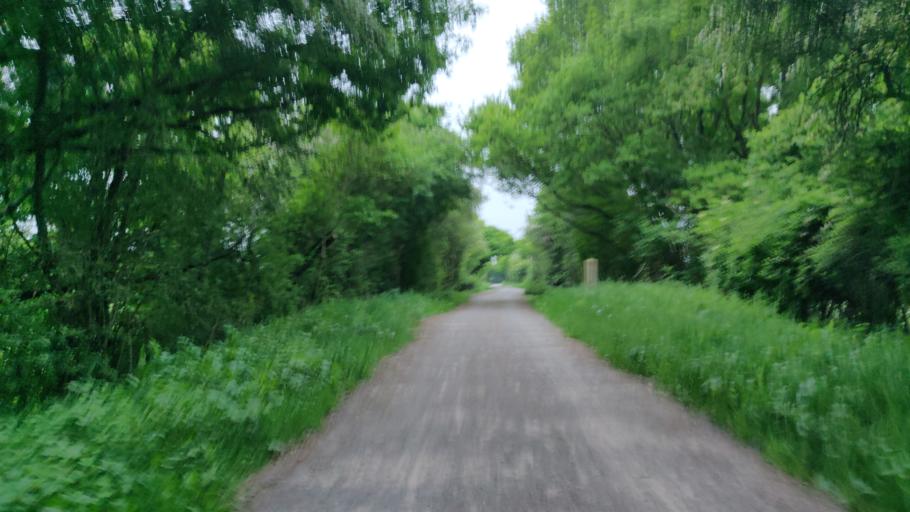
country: GB
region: England
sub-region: West Sussex
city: Partridge Green
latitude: 50.9727
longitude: -0.3158
